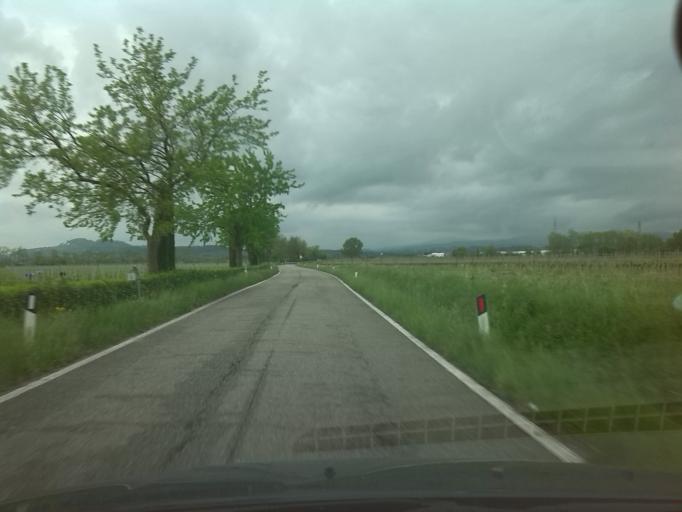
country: IT
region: Friuli Venezia Giulia
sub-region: Provincia di Gorizia
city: Farra d'Isonzo
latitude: 45.9178
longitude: 13.5183
